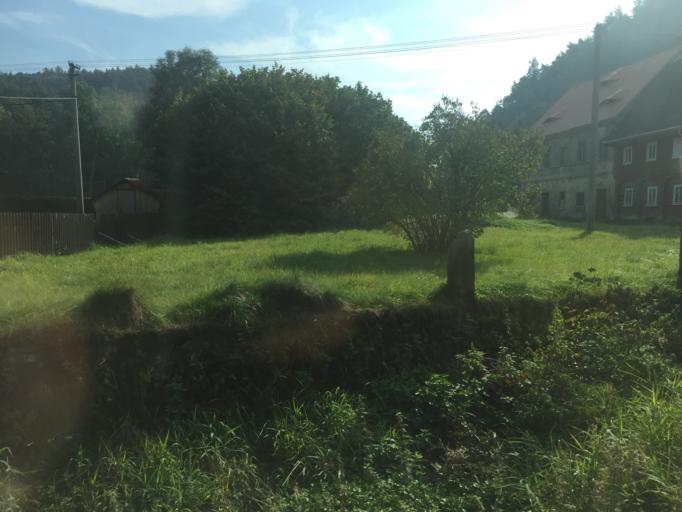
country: CZ
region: Ustecky
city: Ceska Kamenice
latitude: 50.8134
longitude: 14.3510
